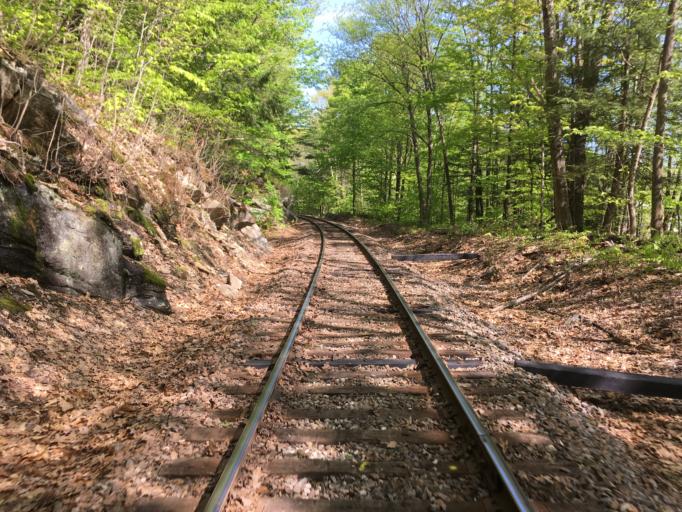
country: US
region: Vermont
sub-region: Windsor County
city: Chester
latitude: 43.3238
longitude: -72.6083
